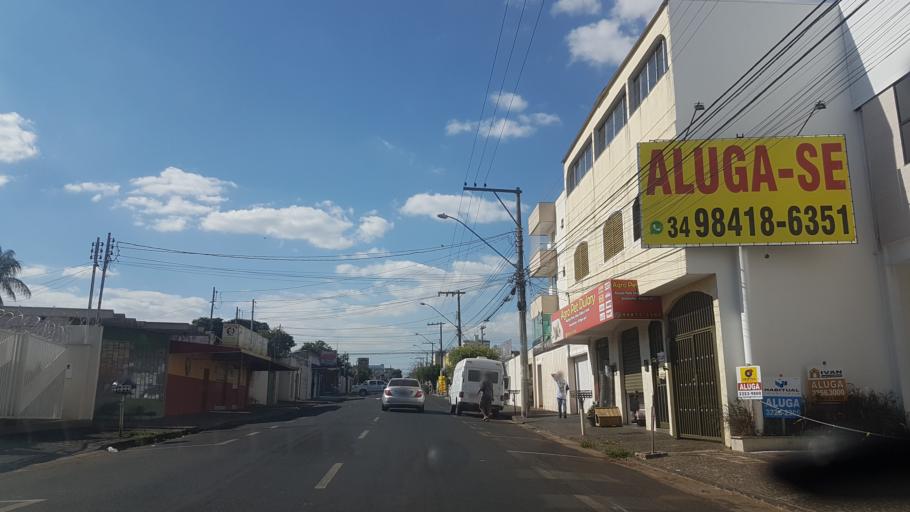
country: BR
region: Minas Gerais
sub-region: Uberlandia
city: Uberlandia
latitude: -18.8963
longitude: -48.2682
